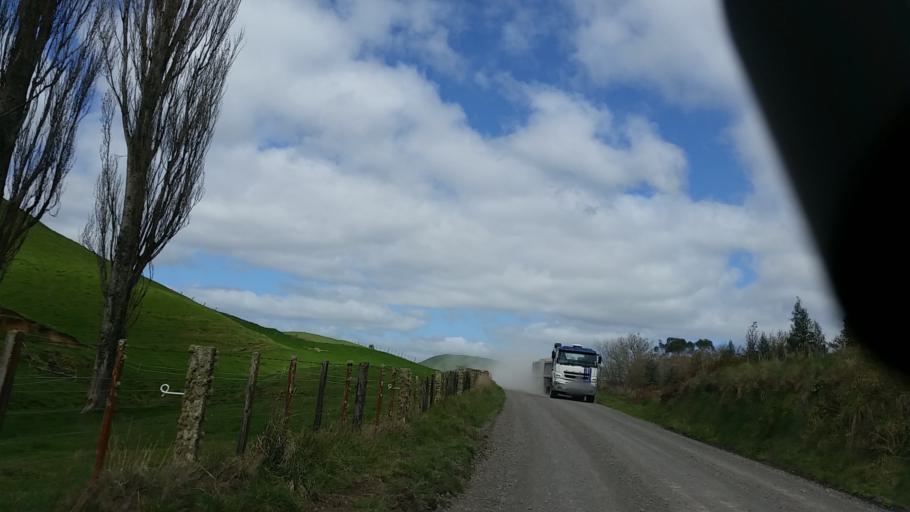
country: NZ
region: Bay of Plenty
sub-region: Rotorua District
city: Rotorua
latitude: -38.3631
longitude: 176.2081
